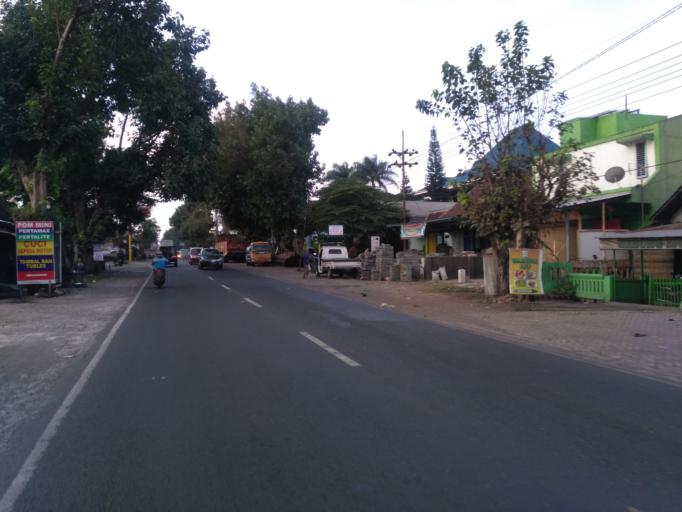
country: ID
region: East Java
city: Kebonsari
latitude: -8.0317
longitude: 112.6141
